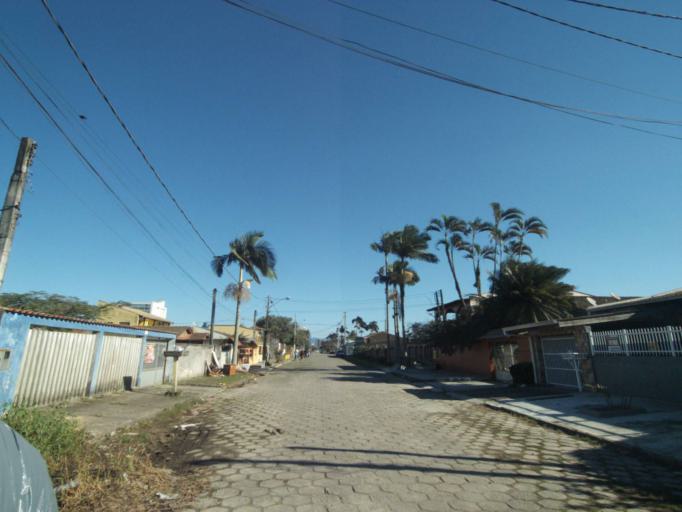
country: BR
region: Parana
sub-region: Paranagua
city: Paranagua
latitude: -25.5105
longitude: -48.5028
